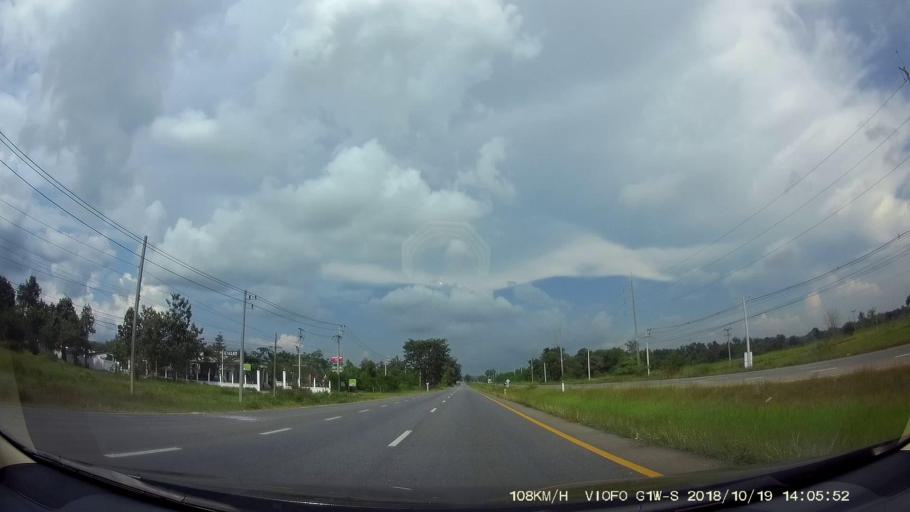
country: TH
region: Chaiyaphum
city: Chaiyaphum
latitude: 15.8803
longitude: 102.0981
